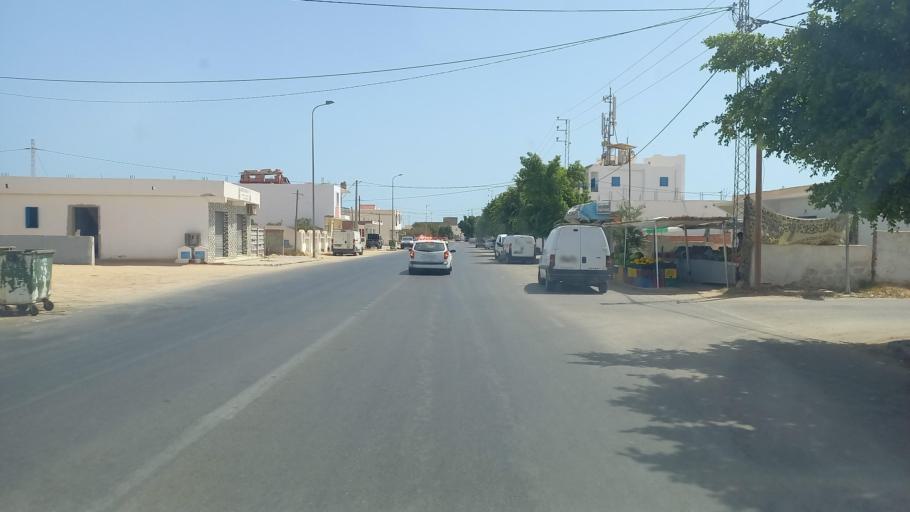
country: TN
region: Madanin
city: Zarzis
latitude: 33.4925
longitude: 11.0739
